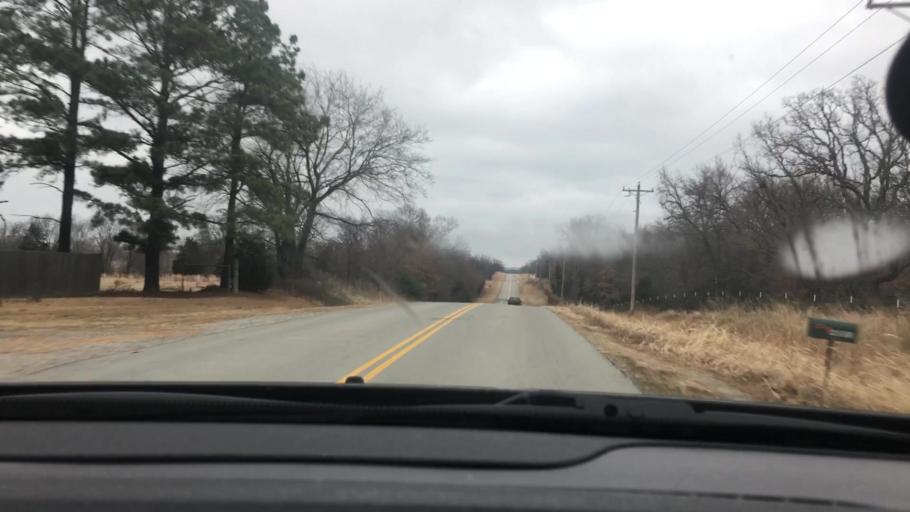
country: US
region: Oklahoma
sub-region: Atoka County
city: Atoka
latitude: 34.3296
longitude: -96.0754
